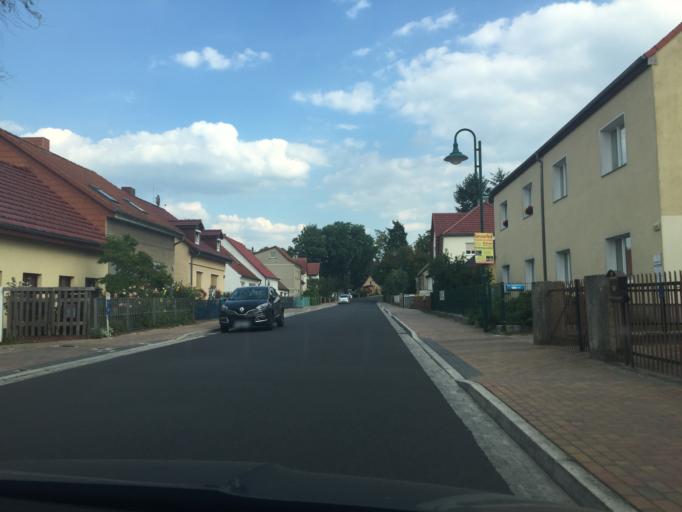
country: DE
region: Brandenburg
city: Erkner
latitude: 52.3866
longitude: 13.7478
